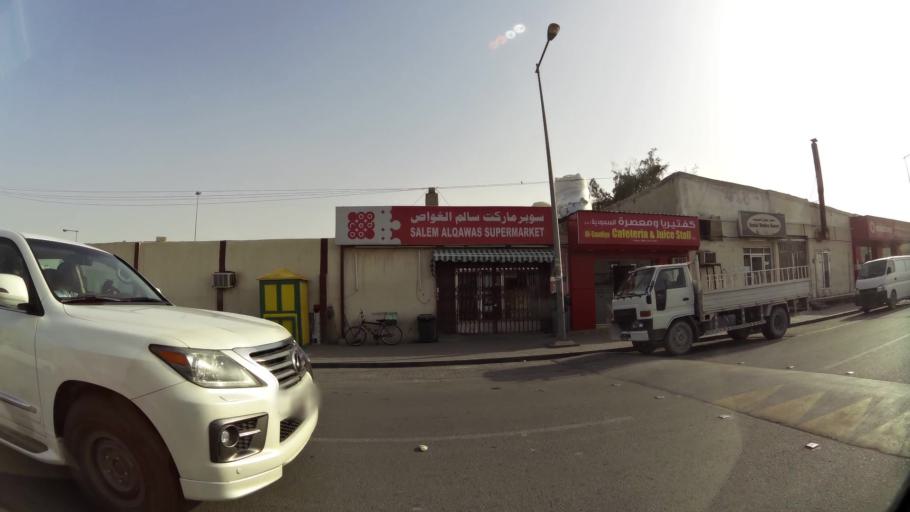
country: QA
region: Baladiyat ar Rayyan
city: Ar Rayyan
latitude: 25.2292
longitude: 51.4364
